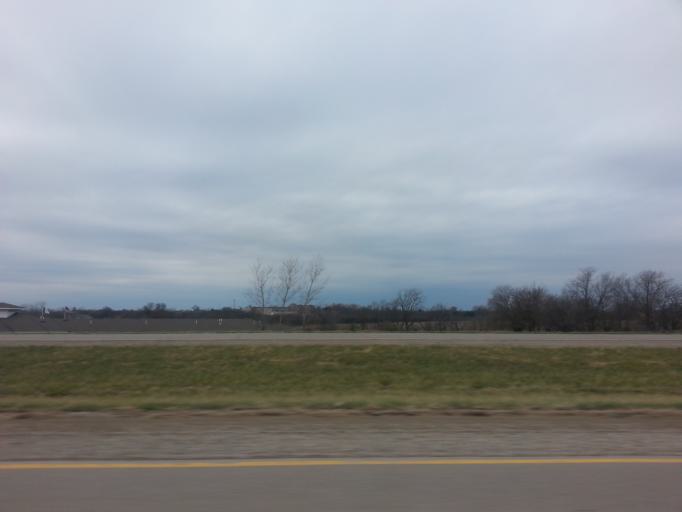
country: US
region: Iowa
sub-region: Henry County
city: Mount Pleasant
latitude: 40.9513
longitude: -91.5246
